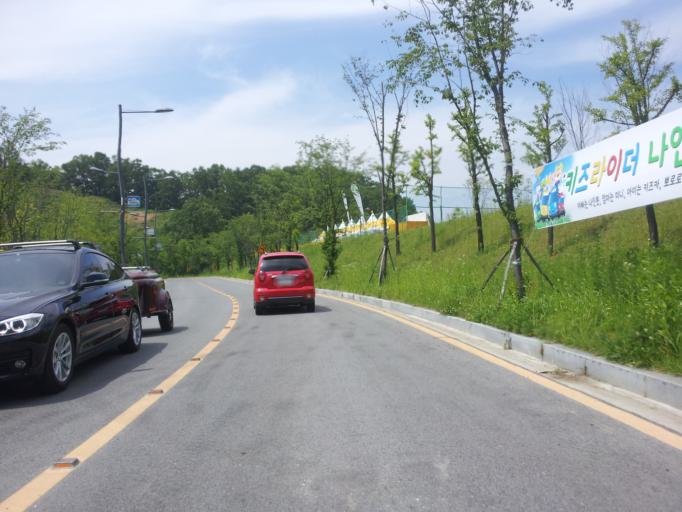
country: KR
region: Daejeon
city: Sintansin
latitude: 36.4568
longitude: 127.4755
